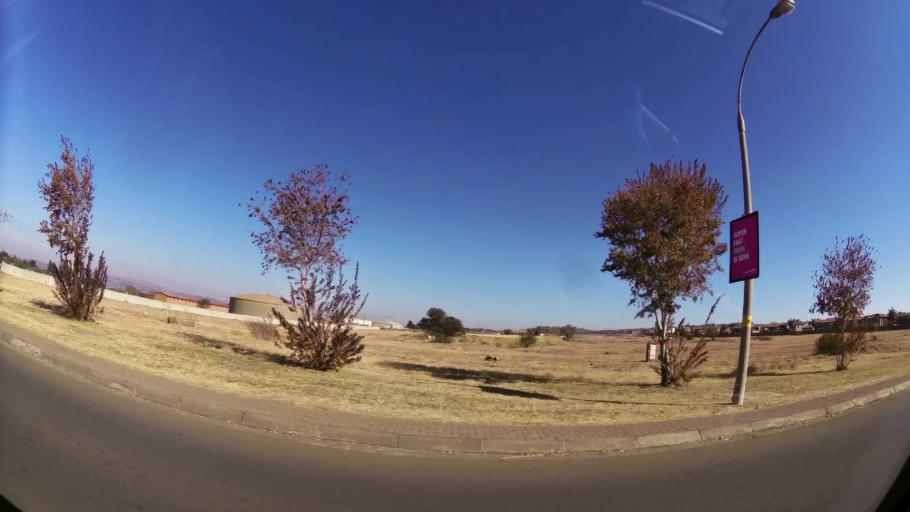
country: ZA
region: Gauteng
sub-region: Ekurhuleni Metropolitan Municipality
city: Germiston
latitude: -26.3037
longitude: 28.0953
